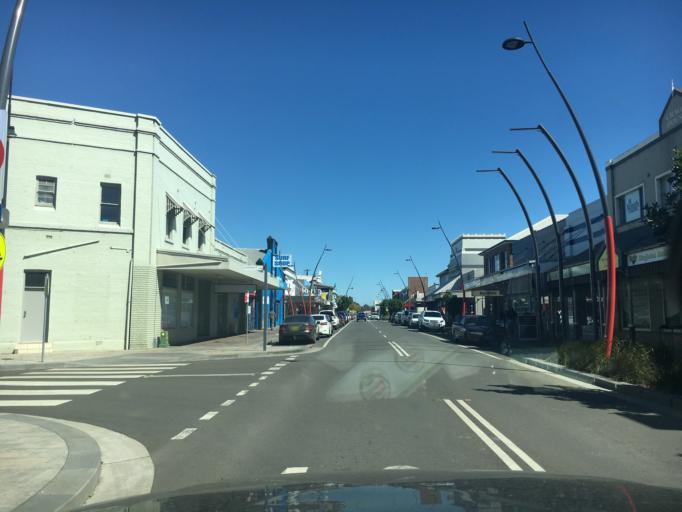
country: AU
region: New South Wales
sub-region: Singleton
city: Singleton
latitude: -32.5655
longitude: 151.1669
